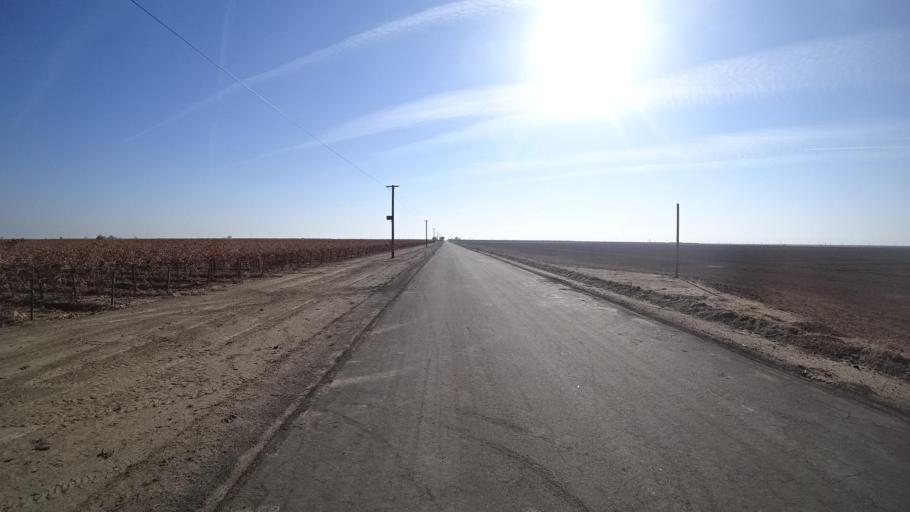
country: US
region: California
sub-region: Kern County
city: Wasco
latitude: 35.6868
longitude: -119.3839
